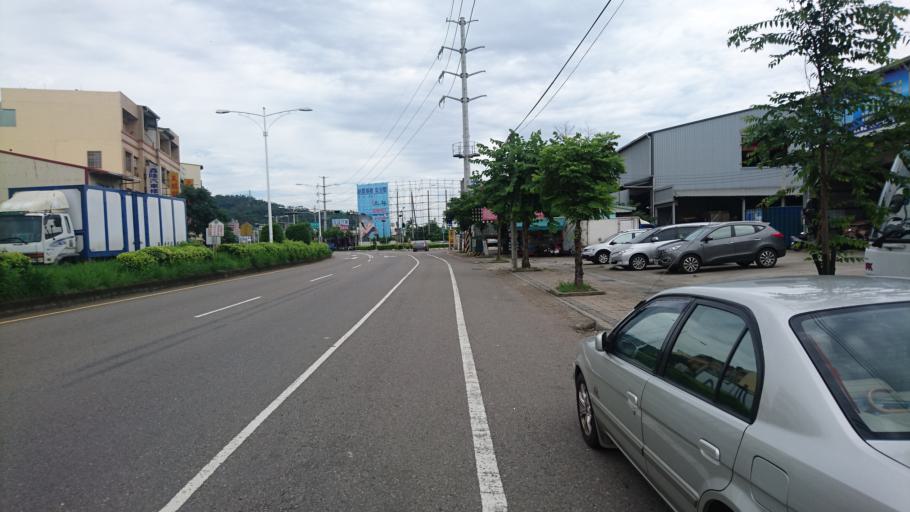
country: TW
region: Taiwan
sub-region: Taichung City
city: Taichung
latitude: 24.0605
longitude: 120.6952
